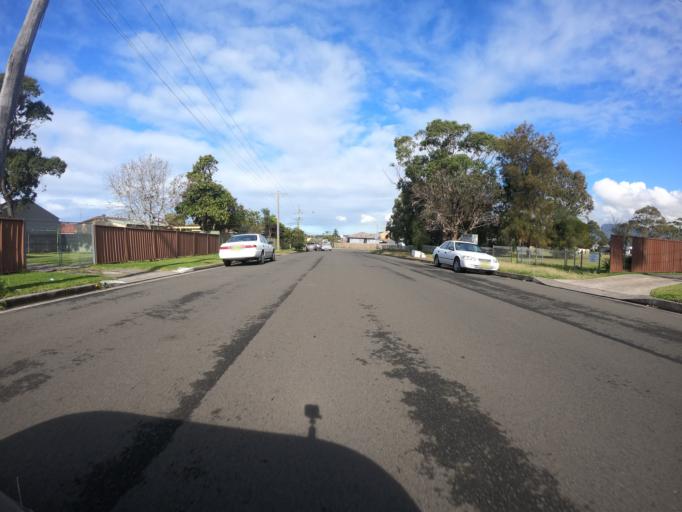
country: AU
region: New South Wales
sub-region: Wollongong
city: East Corrimal
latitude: -34.3758
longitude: 150.9125
